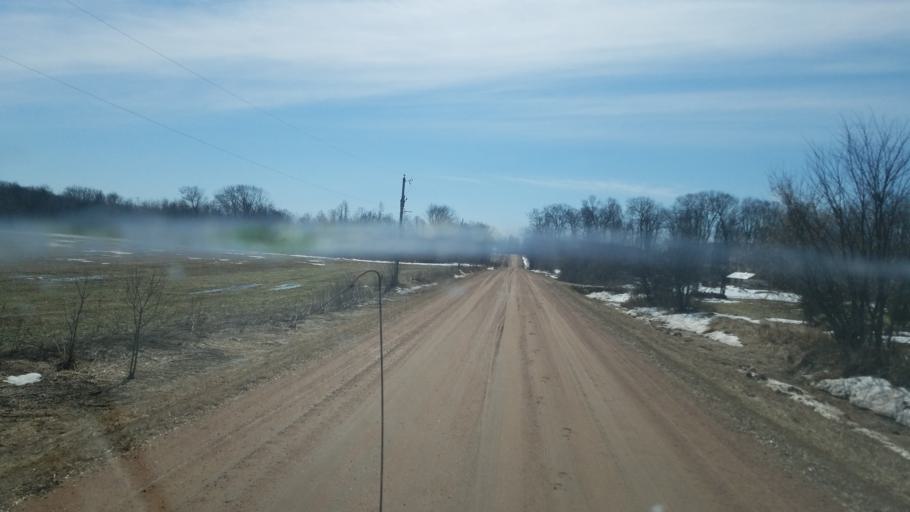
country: US
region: Wisconsin
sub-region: Clark County
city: Loyal
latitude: 44.6323
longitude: -90.4072
